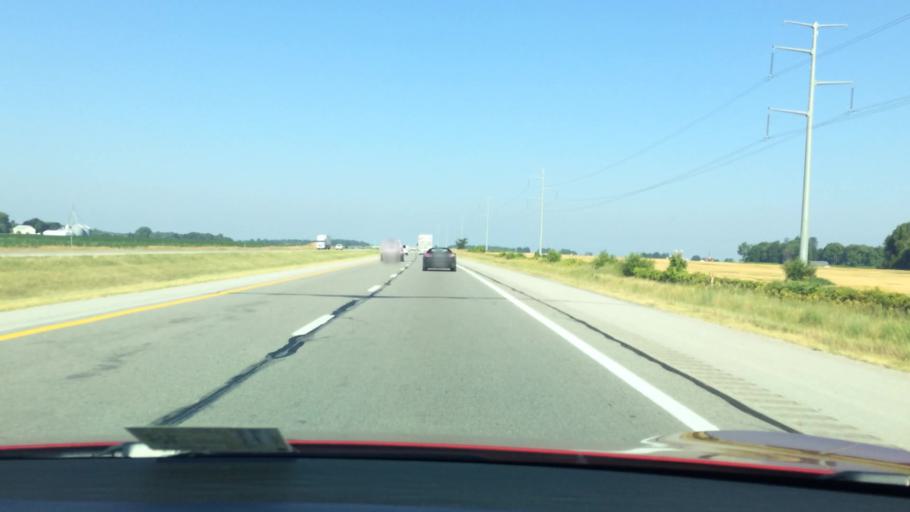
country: US
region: Ohio
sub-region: Fulton County
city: Swanton
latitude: 41.5999
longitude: -83.9452
